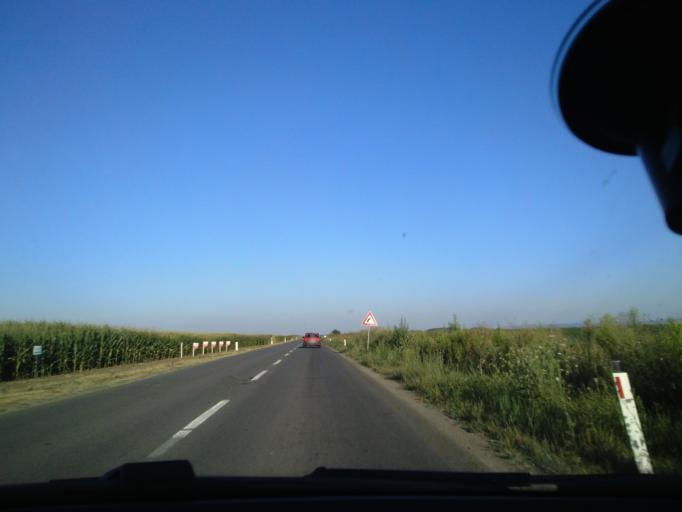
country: RS
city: Maglic
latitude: 45.3858
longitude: 19.5024
